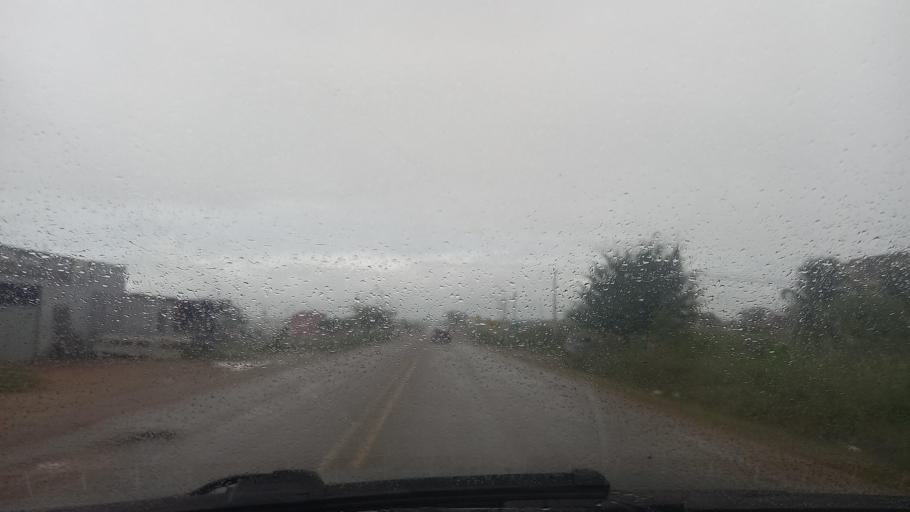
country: BR
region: Bahia
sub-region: Paulo Afonso
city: Paulo Afonso
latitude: -9.3594
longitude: -38.2758
